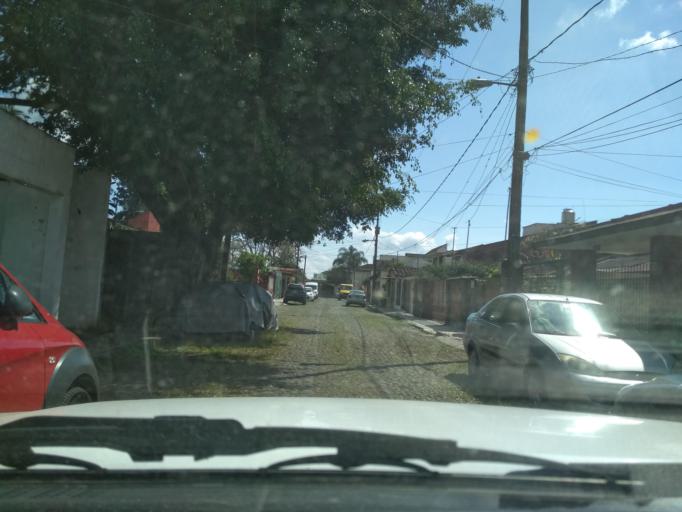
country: MX
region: Veracruz
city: Coatepec
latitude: 19.4503
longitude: -96.9506
